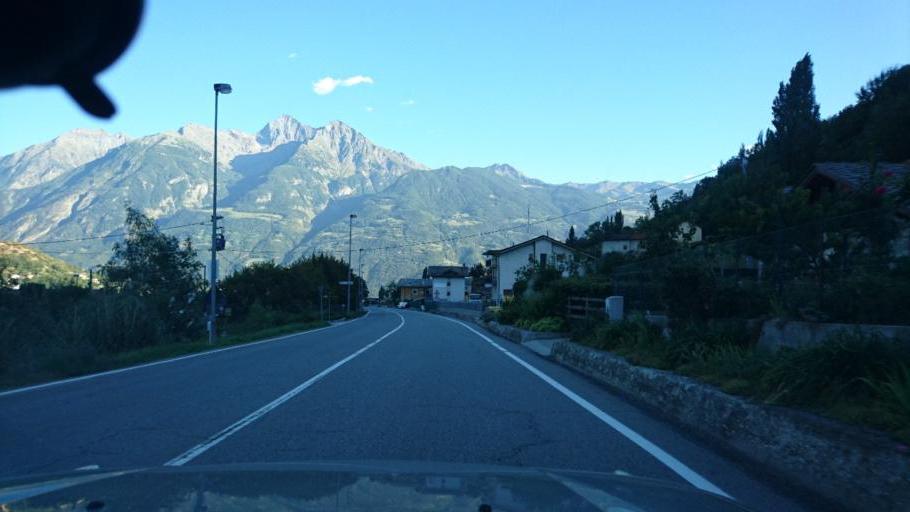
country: IT
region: Aosta Valley
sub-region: Valle d'Aosta
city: Aosta
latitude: 45.7590
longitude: 7.3155
